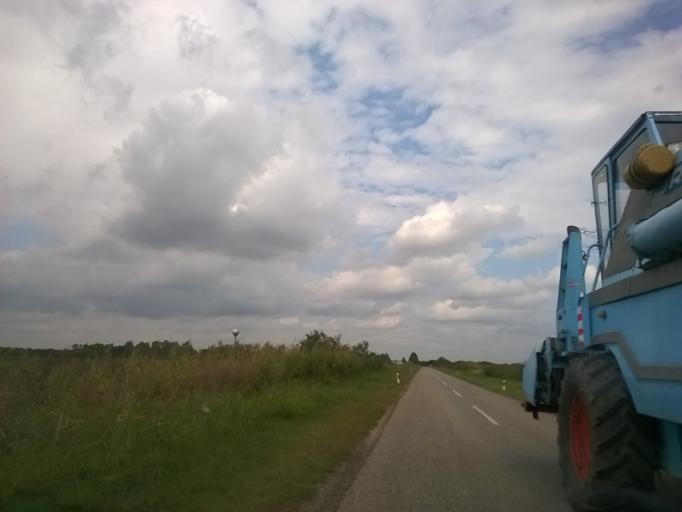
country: RS
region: Autonomna Pokrajina Vojvodina
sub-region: Juznobanatski Okrug
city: Plandiste
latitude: 45.2093
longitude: 21.1051
